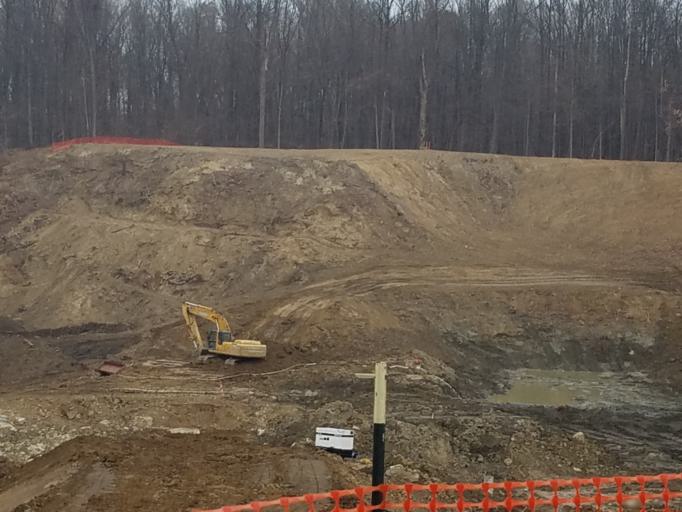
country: US
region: Ohio
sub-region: Morrow County
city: Mount Gilead
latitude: 40.5487
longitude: -82.8204
